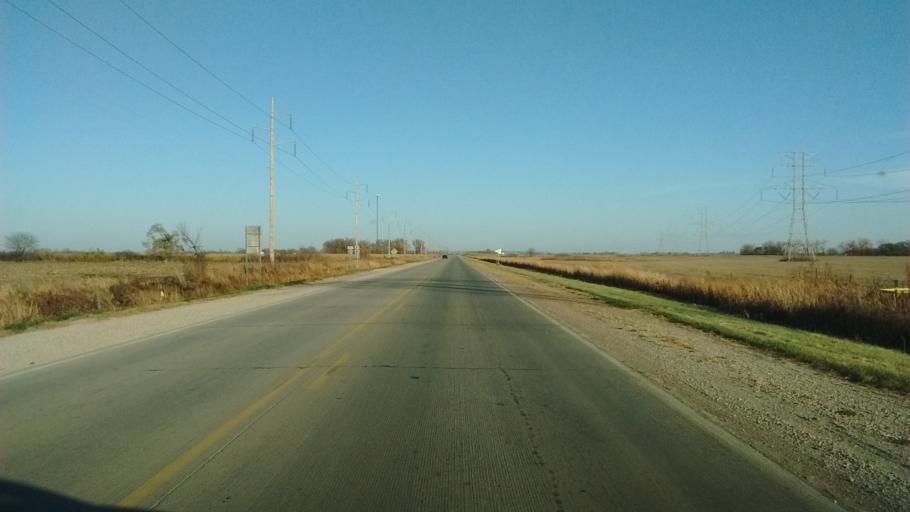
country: US
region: Iowa
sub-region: Woodbury County
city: Sergeant Bluff
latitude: 42.3301
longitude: -96.3475
